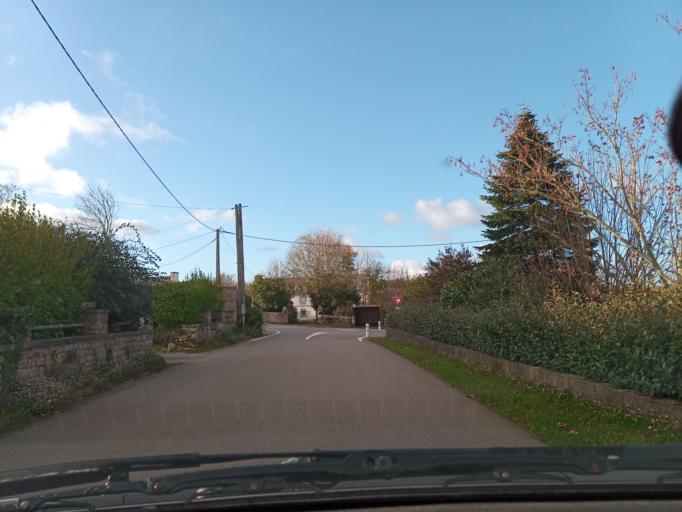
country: FR
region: Brittany
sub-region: Departement du Finistere
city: Esquibien
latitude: 48.0118
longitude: -4.5656
